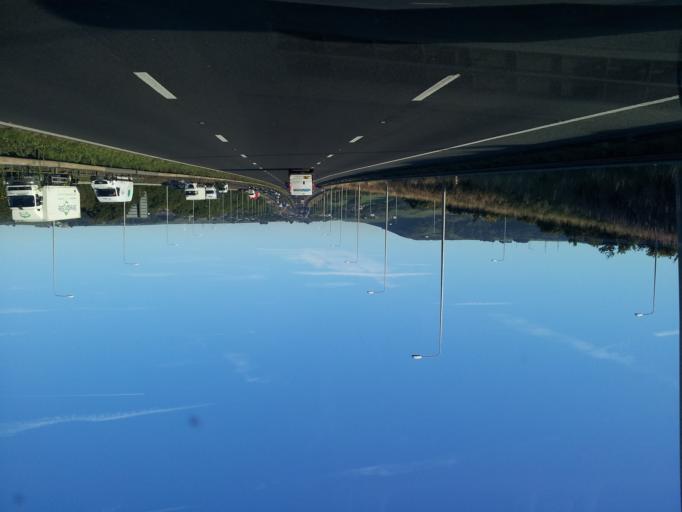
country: GB
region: England
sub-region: Calderdale
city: Elland
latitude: 53.6591
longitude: -1.8633
